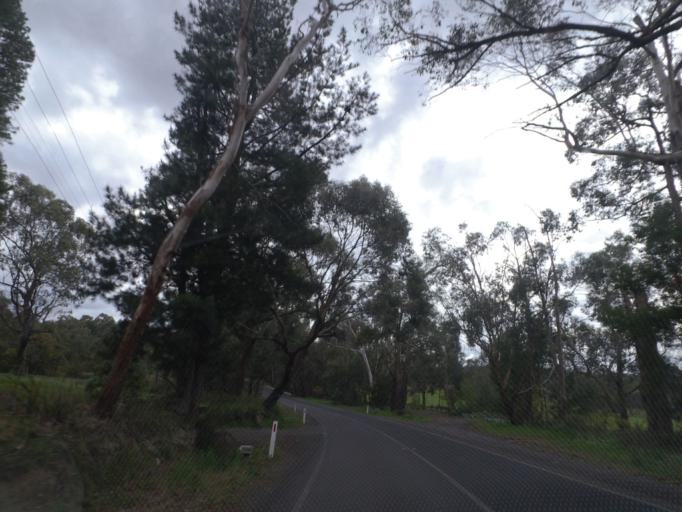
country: AU
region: Victoria
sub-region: Yarra Ranges
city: Mount Evelyn
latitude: -37.7677
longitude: 145.4169
